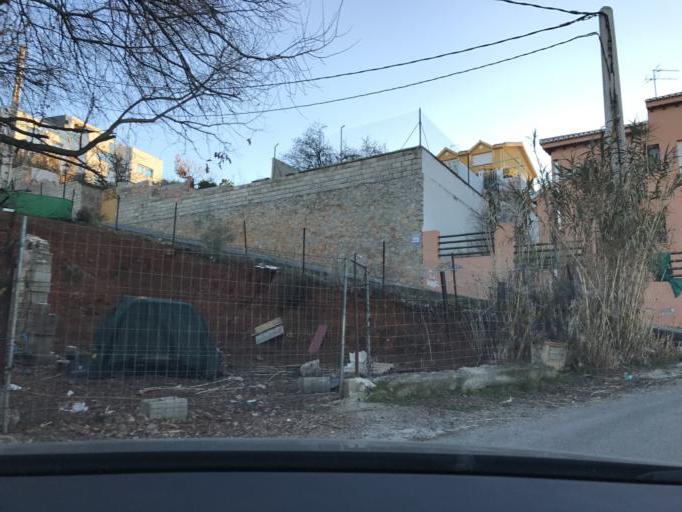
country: ES
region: Andalusia
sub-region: Provincia de Granada
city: Huetor Vega
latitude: 37.1559
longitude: -3.5638
